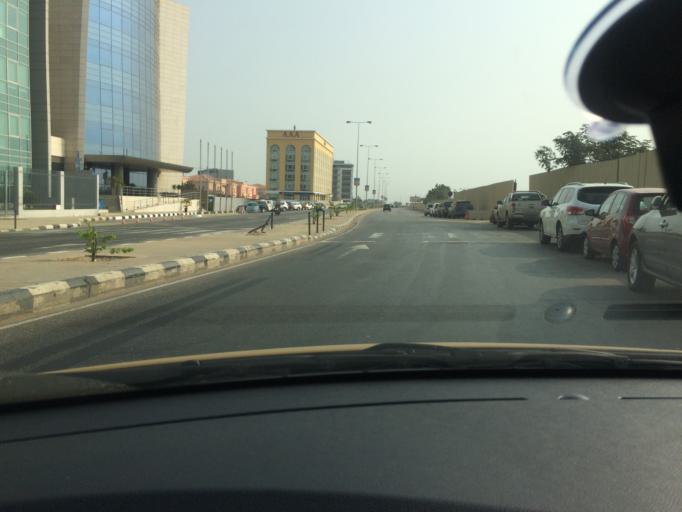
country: AO
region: Luanda
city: Luanda
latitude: -8.8148
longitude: 13.2208
